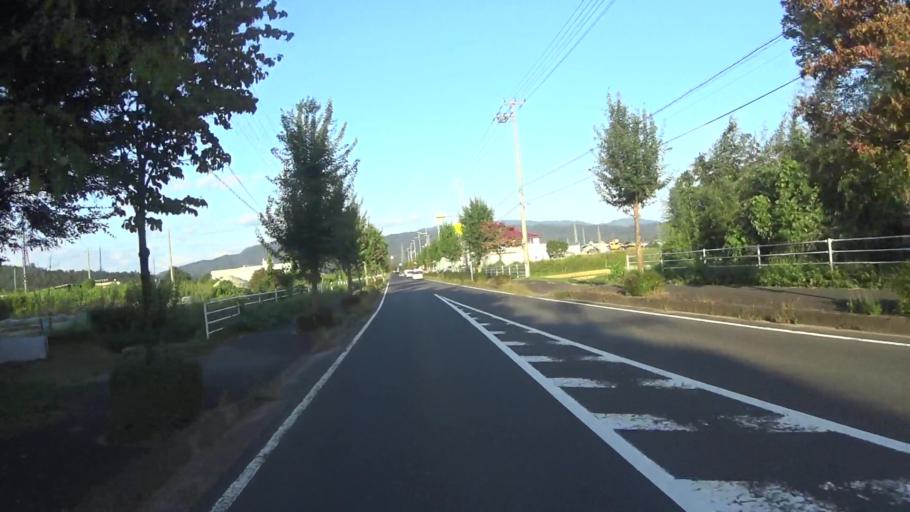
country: JP
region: Kyoto
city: Miyazu
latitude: 35.6075
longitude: 135.0592
